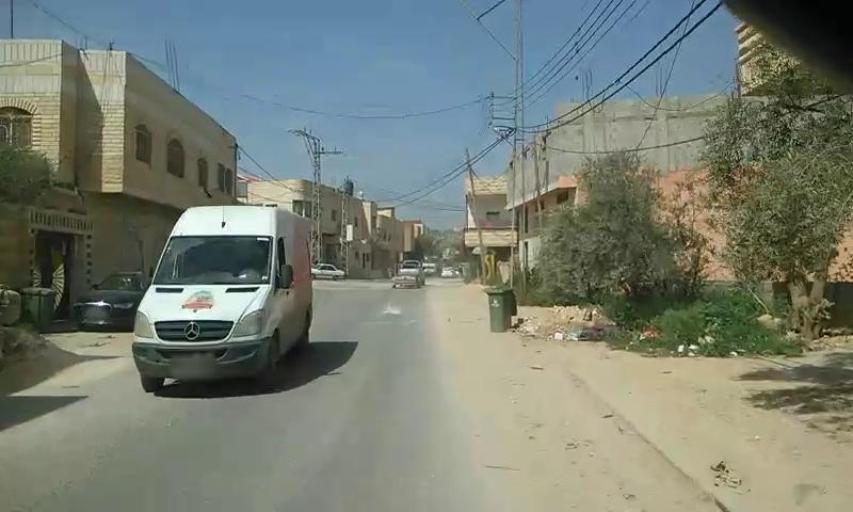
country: PS
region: West Bank
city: Qabatiyah
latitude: 32.4072
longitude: 35.2876
